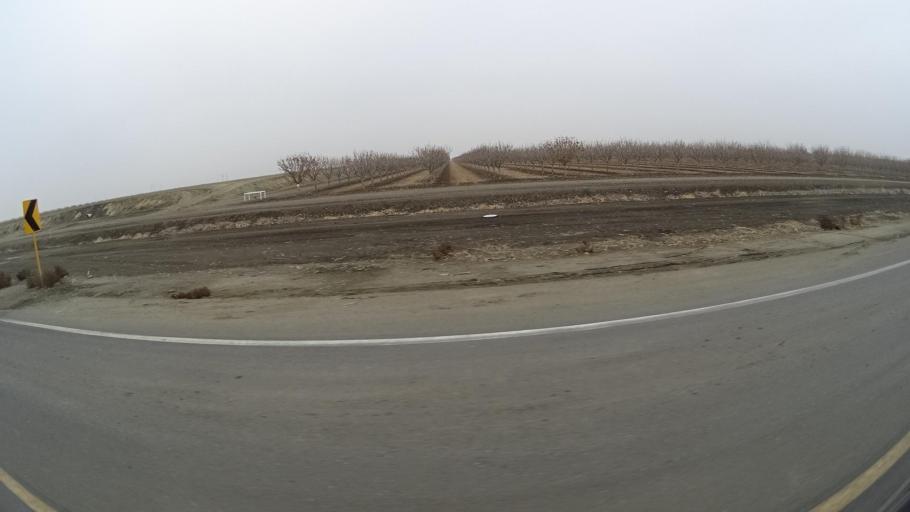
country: US
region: California
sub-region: Kern County
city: Buttonwillow
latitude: 35.3690
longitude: -119.4737
